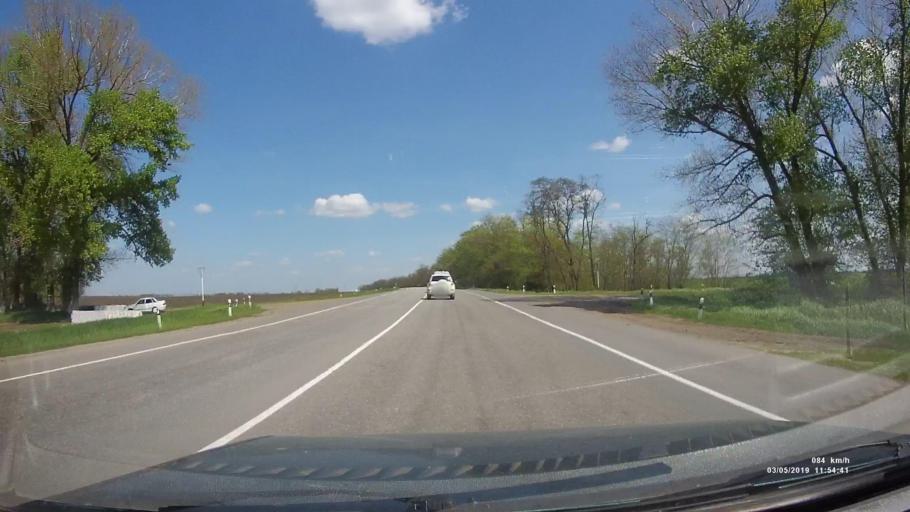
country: RU
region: Rostov
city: Bagayevskaya
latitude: 47.1723
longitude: 40.2835
